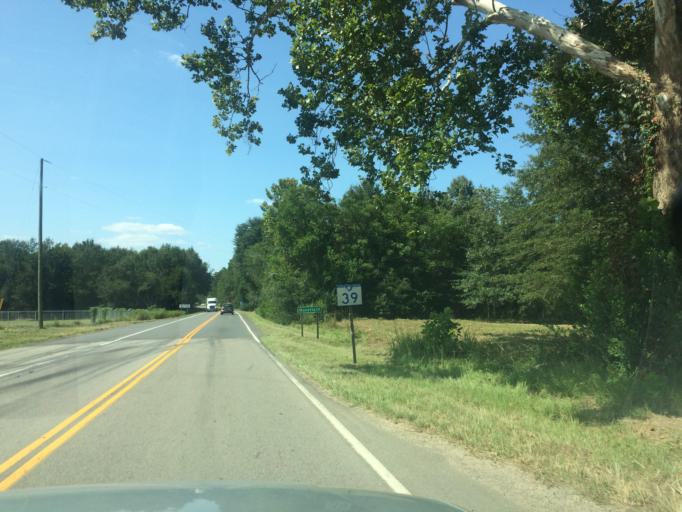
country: US
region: South Carolina
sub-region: Lexington County
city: Batesburg-Leesville
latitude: 33.7009
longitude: -81.4804
